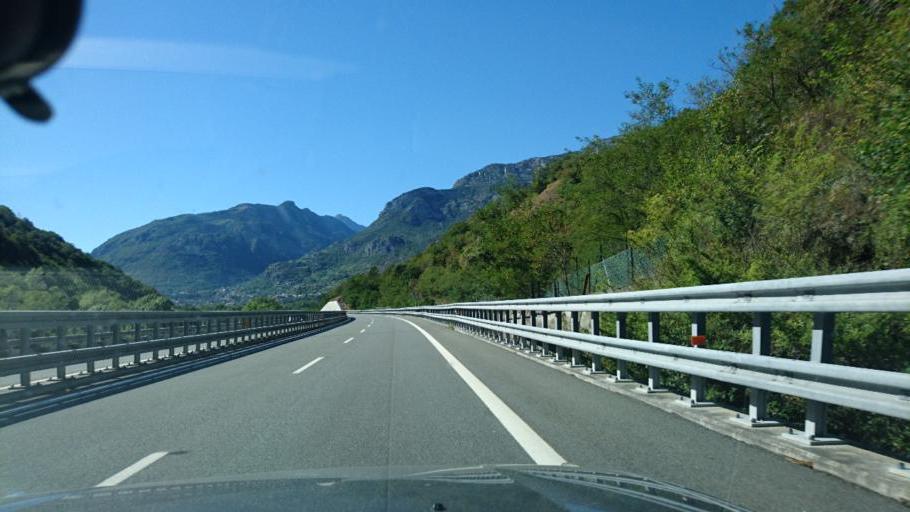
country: IT
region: Aosta Valley
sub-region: Valle d'Aosta
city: Saint-Vincent
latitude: 45.7378
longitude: 7.6541
